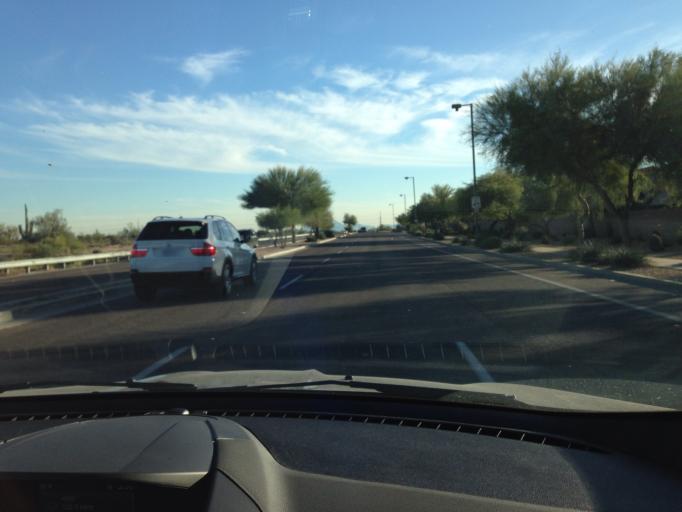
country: US
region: Arizona
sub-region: Maricopa County
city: Cave Creek
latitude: 33.7227
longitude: -111.9776
